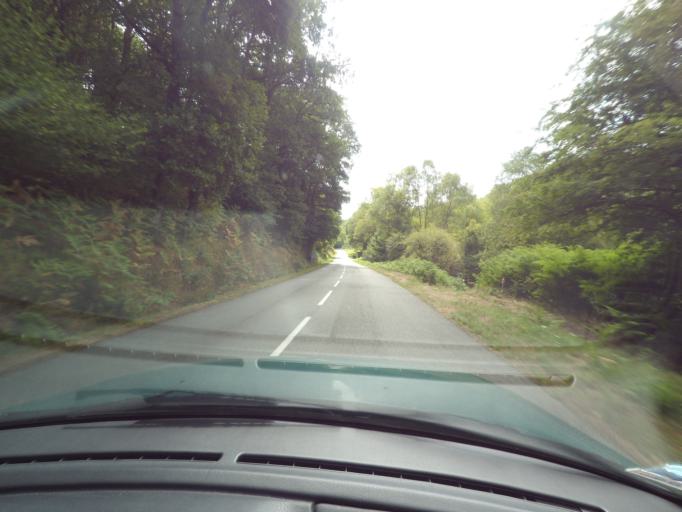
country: FR
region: Limousin
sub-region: Departement de la Haute-Vienne
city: Eymoutiers
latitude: 45.7147
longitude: 1.8429
